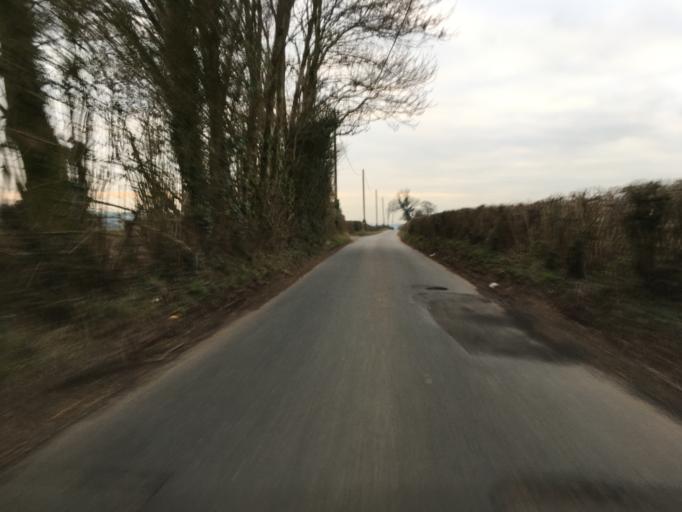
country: GB
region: Wales
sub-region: Newport
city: Marshfield
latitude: 51.5730
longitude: -3.0711
